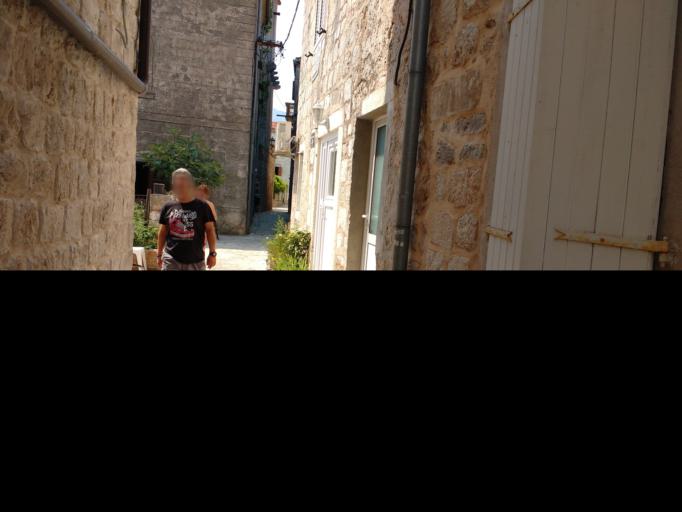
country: ME
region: Kotor
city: Risan
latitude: 42.4852
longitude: 18.7008
